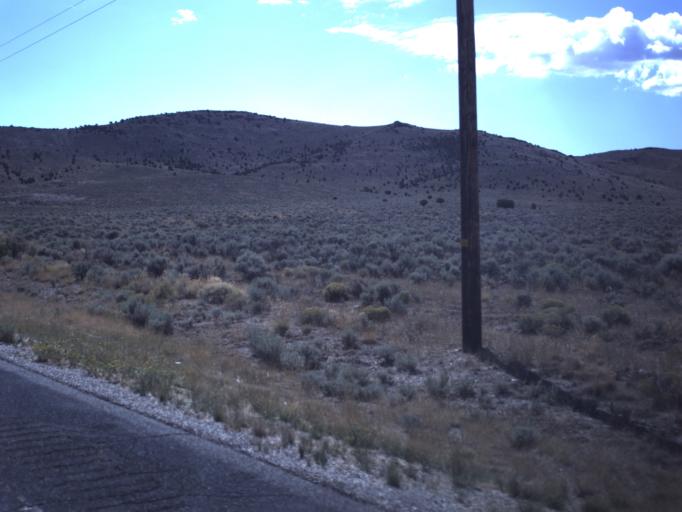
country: US
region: Utah
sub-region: Utah County
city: Eagle Mountain
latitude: 40.0736
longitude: -112.3791
